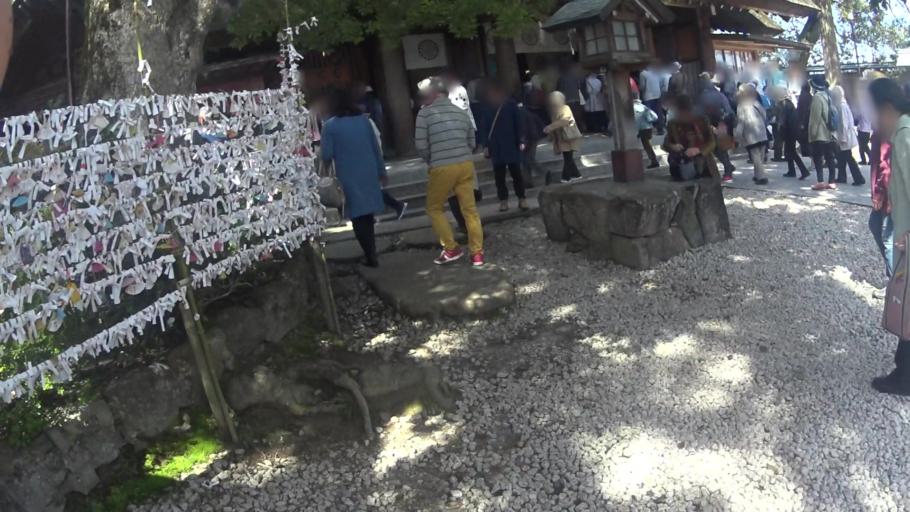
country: JP
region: Kyoto
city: Miyazu
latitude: 35.5827
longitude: 135.1965
